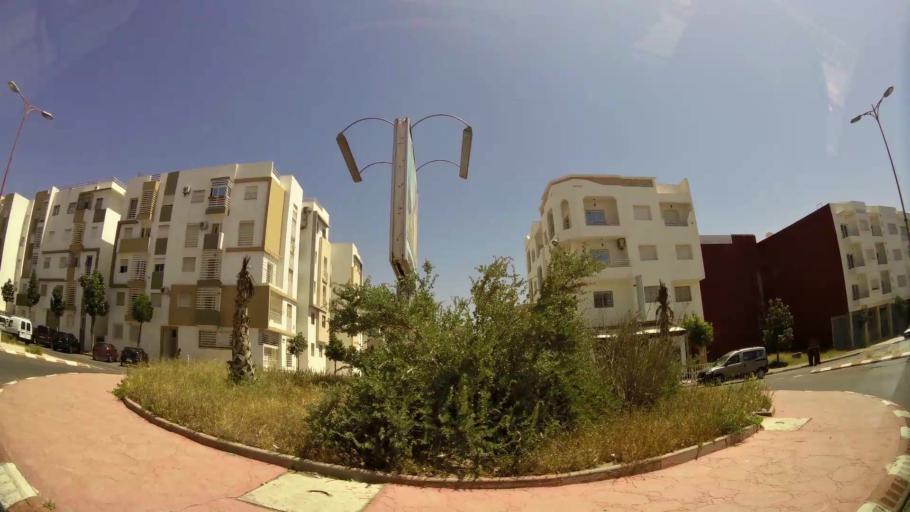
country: MA
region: Oued ed Dahab-Lagouira
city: Dakhla
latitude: 30.4322
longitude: -9.5566
